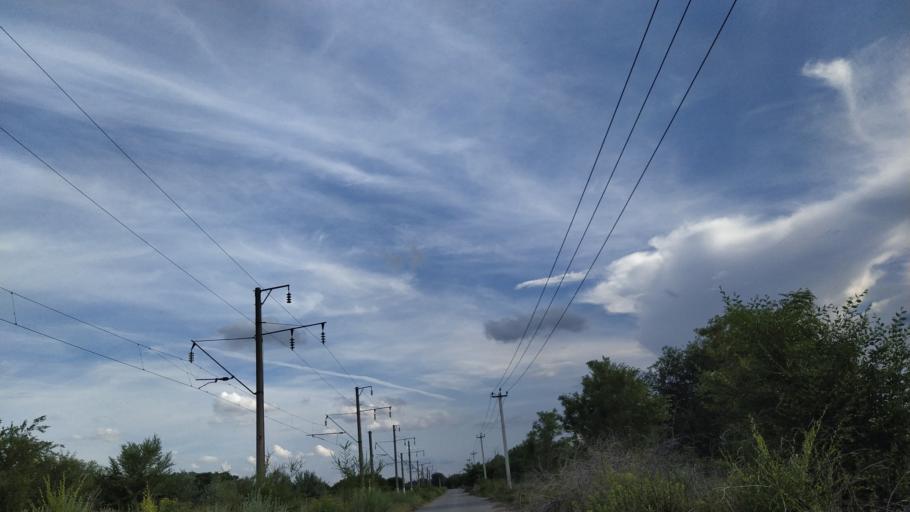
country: RU
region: Rostov
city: Bataysk
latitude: 47.1138
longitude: 39.7114
